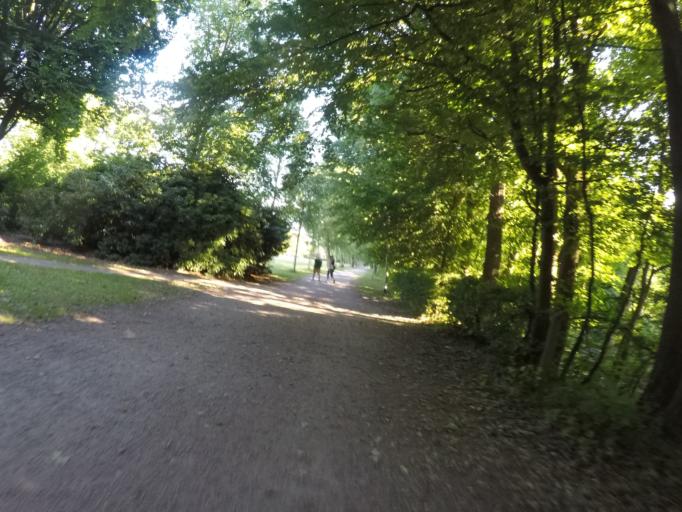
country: DE
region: Hamburg
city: Fuhlsbuettel
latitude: 53.6454
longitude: 10.0175
